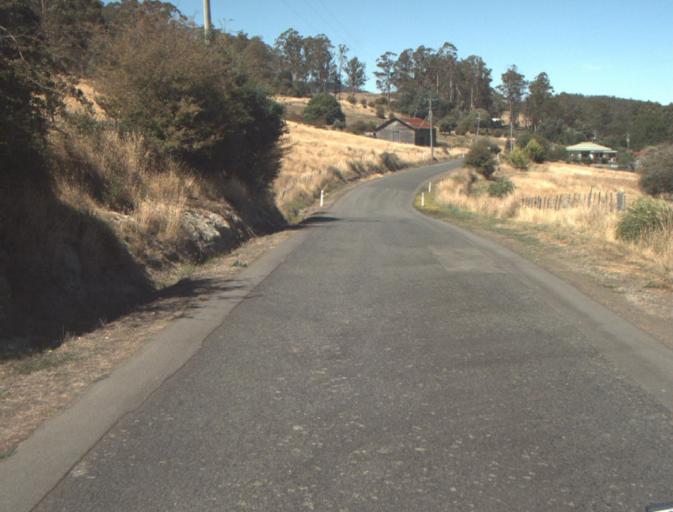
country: AU
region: Tasmania
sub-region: Launceston
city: Newstead
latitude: -41.3514
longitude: 147.3037
